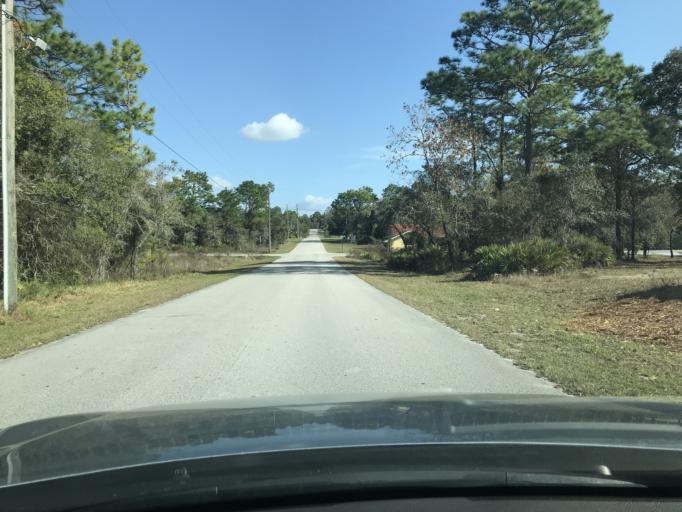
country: US
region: Florida
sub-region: Hernando County
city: North Weeki Wachee
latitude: 28.5475
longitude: -82.5498
